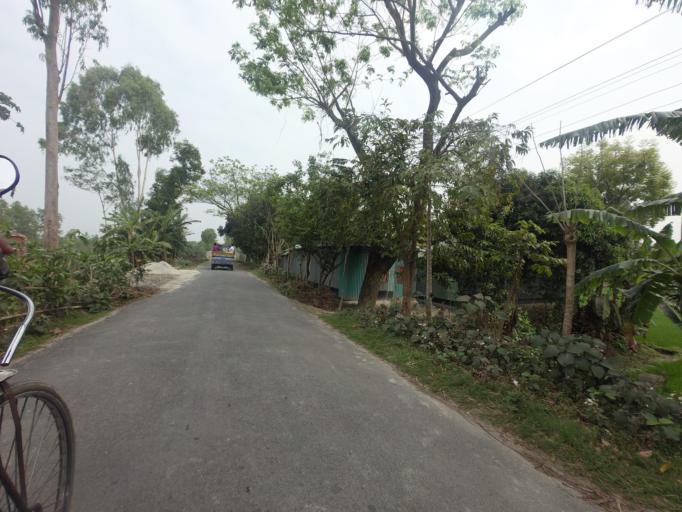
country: BD
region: Rajshahi
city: Sirajganj
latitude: 24.3643
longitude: 89.6707
